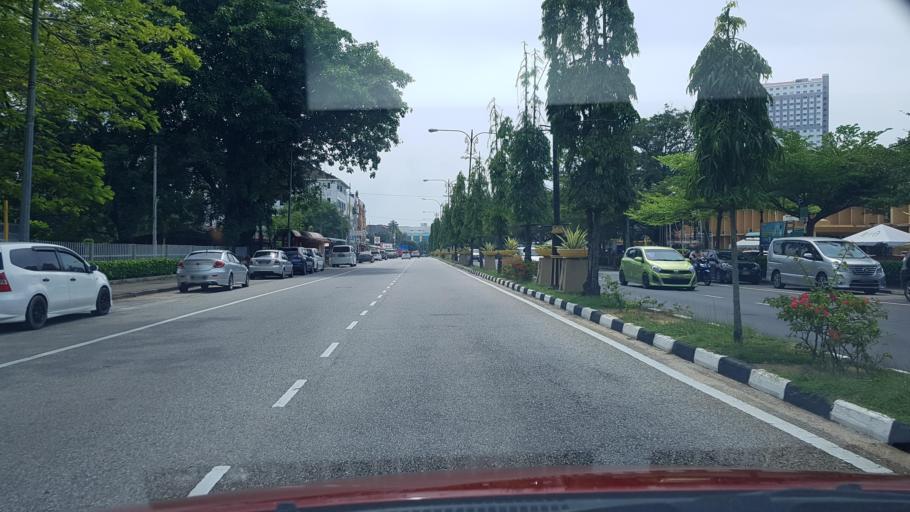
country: MY
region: Terengganu
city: Kuala Terengganu
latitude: 5.3252
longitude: 103.1491
